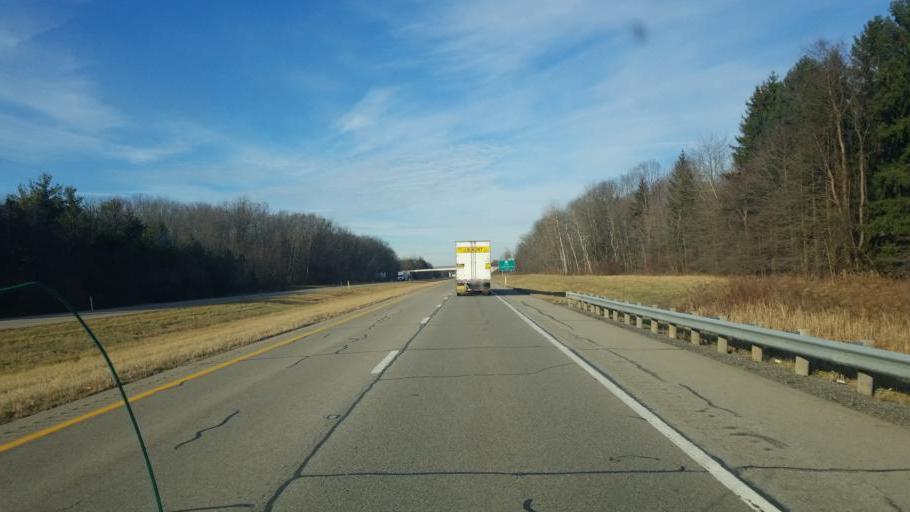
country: US
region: Ohio
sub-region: Ashtabula County
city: Orwell
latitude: 41.5165
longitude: -80.7132
